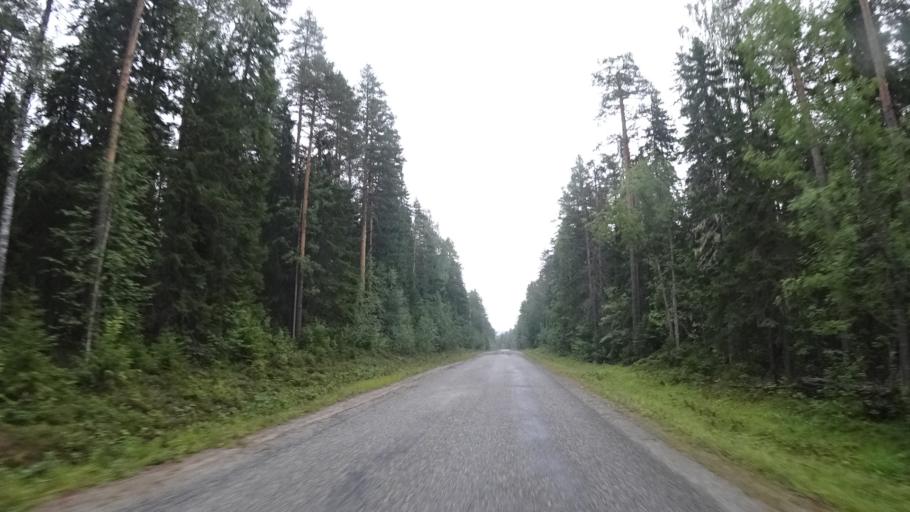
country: FI
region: North Karelia
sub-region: Joensuu
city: Ilomantsi
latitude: 63.2276
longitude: 30.8509
